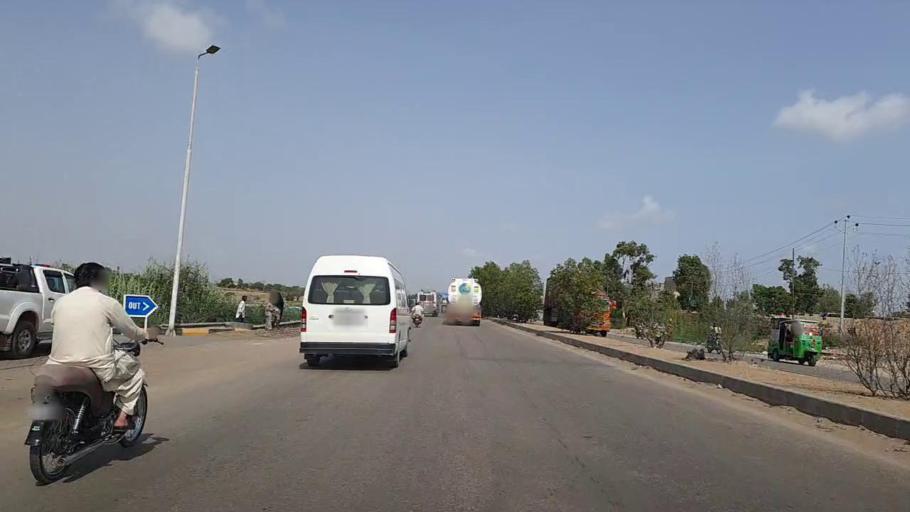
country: PK
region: Sindh
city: Malir Cantonment
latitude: 24.8598
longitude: 67.3372
